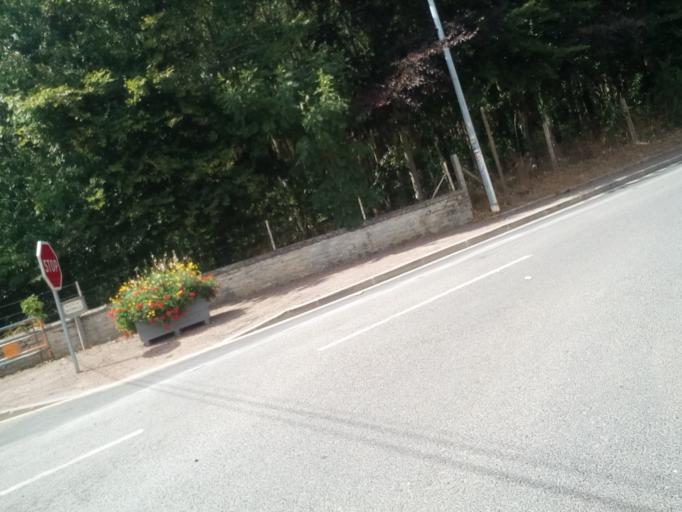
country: FR
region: Lower Normandy
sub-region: Departement du Calvados
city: Creully
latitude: 49.2906
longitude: -0.5695
